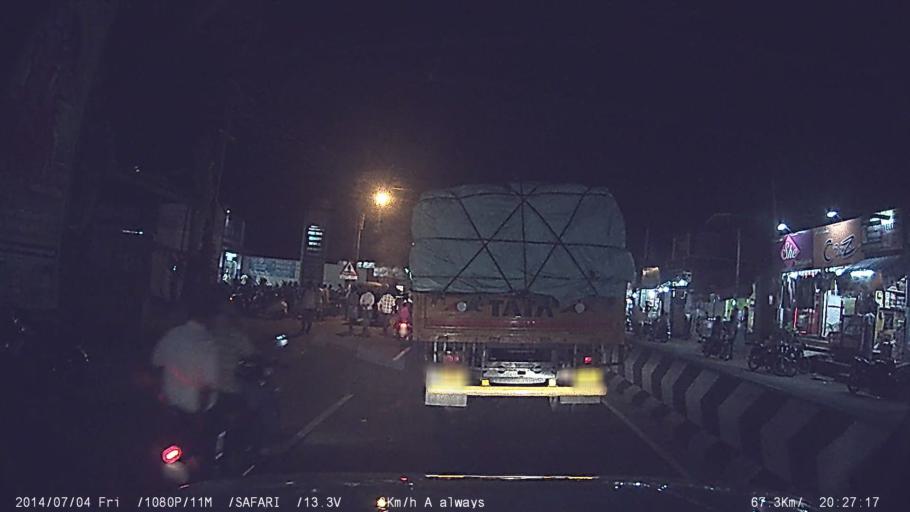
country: IN
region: Tamil Nadu
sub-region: Coimbatore
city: Perur
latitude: 10.9646
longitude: 76.9553
